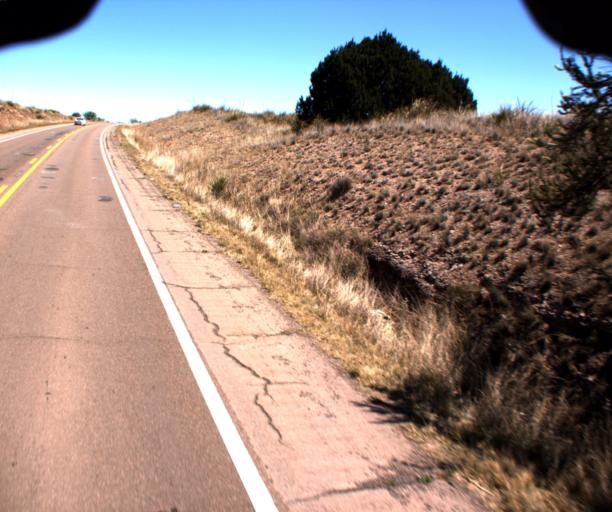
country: US
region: Arizona
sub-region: Pima County
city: Corona de Tucson
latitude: 31.6745
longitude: -110.6687
